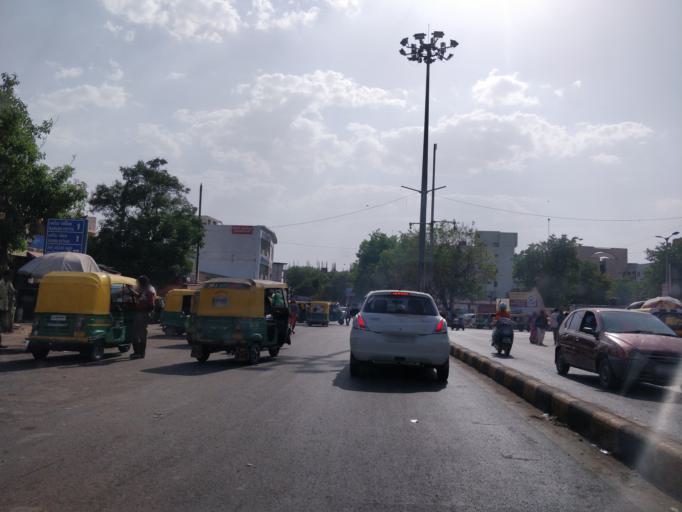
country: IN
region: Gujarat
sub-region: Ahmadabad
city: Naroda
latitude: 23.0748
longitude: 72.6566
